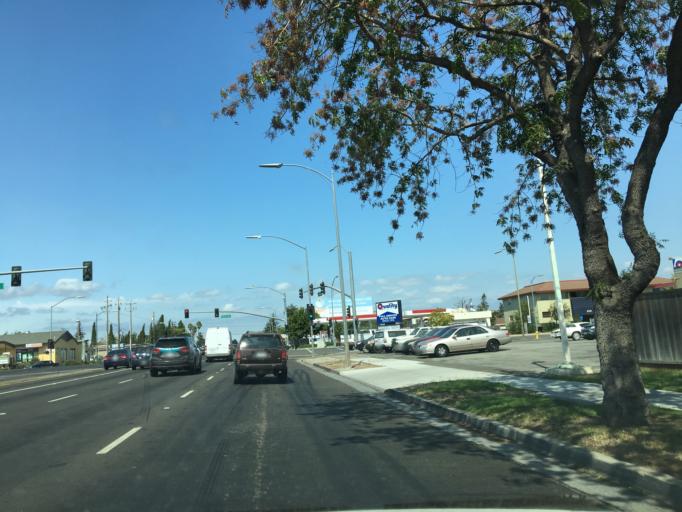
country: US
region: California
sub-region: Santa Clara County
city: Cambrian Park
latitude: 37.2658
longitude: -121.9404
